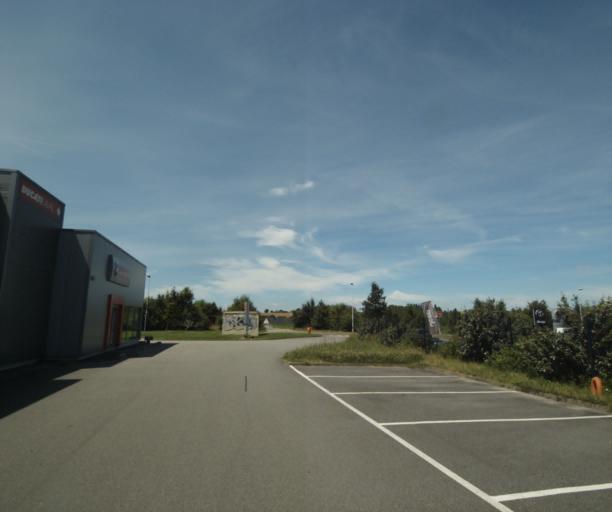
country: FR
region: Pays de la Loire
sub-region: Departement de la Mayenne
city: Change
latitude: 48.0842
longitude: -0.7930
